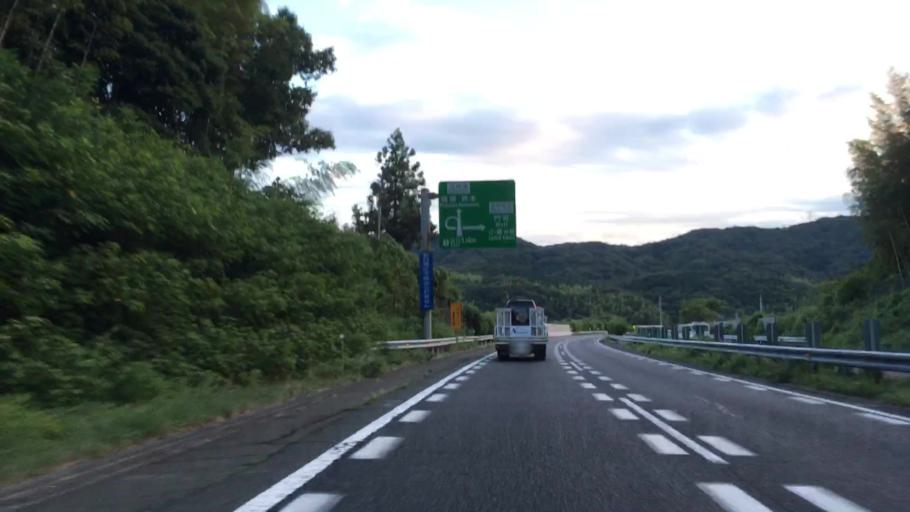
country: JP
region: Yamaguchi
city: Shimonoseki
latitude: 33.9320
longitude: 130.9956
